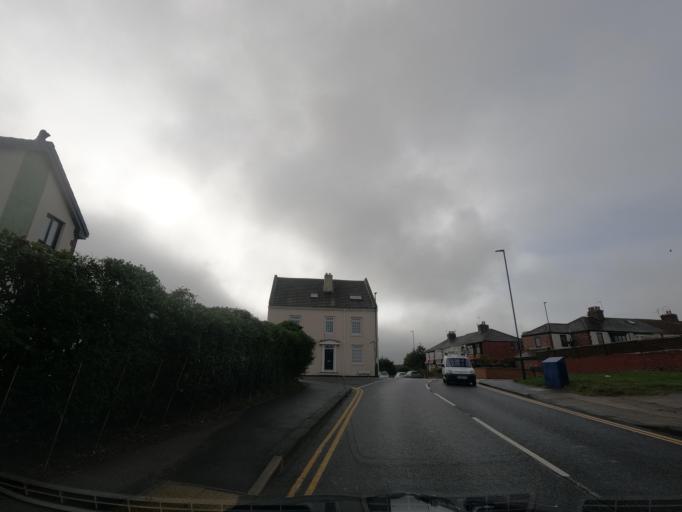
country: GB
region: England
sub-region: Redcar and Cleveland
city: Redcar
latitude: 54.6177
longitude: -1.0849
